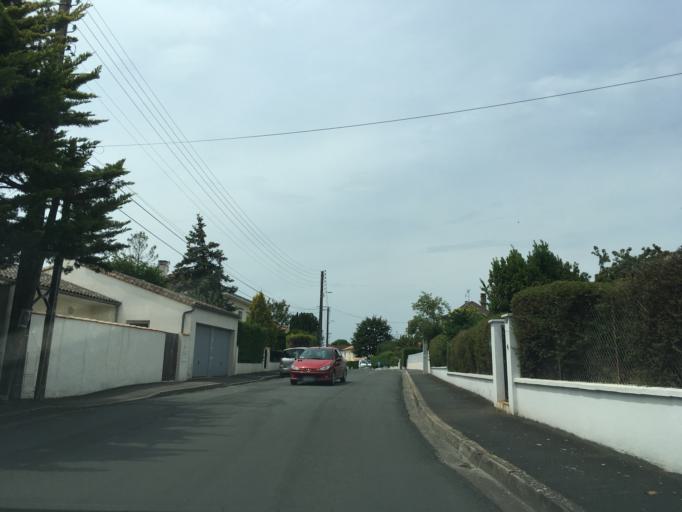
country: FR
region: Poitou-Charentes
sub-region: Departement des Deux-Sevres
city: Niort
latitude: 46.3185
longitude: -0.4740
